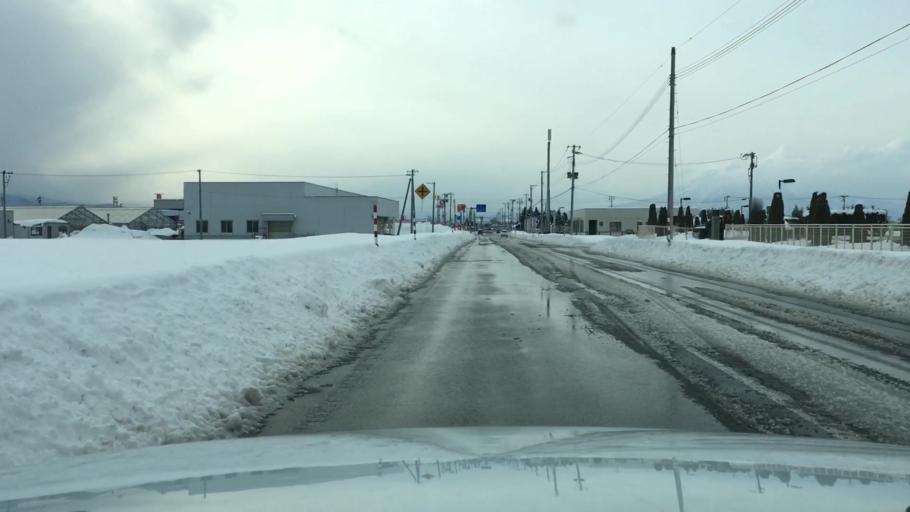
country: JP
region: Aomori
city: Kuroishi
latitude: 40.5917
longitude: 140.5727
